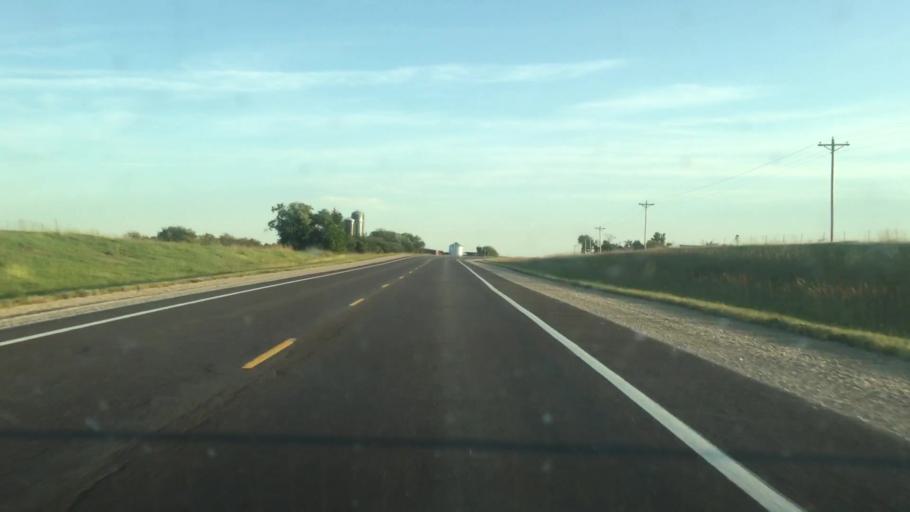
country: US
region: Kansas
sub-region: Atchison County
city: Atchison
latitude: 39.4508
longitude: -95.1010
